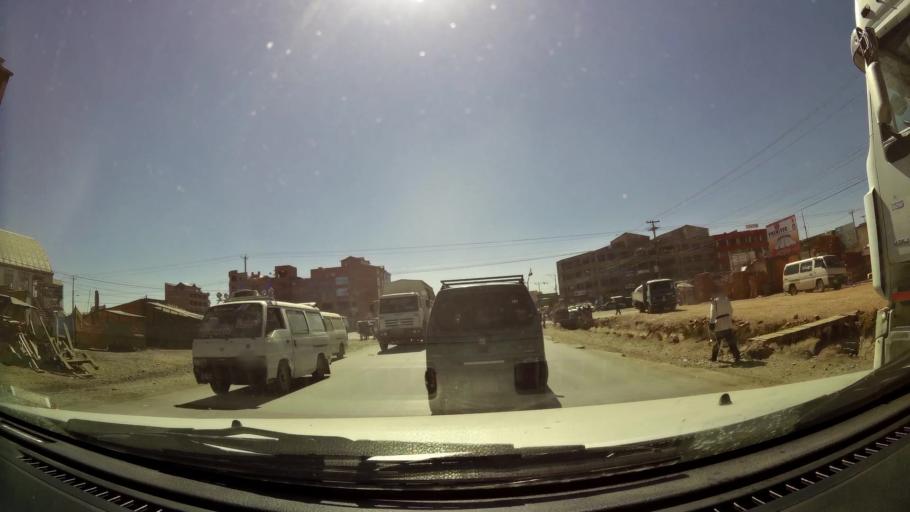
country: BO
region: La Paz
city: La Paz
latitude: -16.5432
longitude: -68.1986
